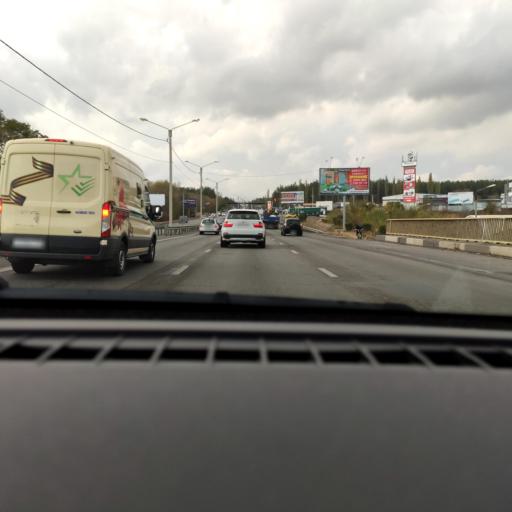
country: RU
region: Voronezj
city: Pridonskoy
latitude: 51.6699
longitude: 39.1229
